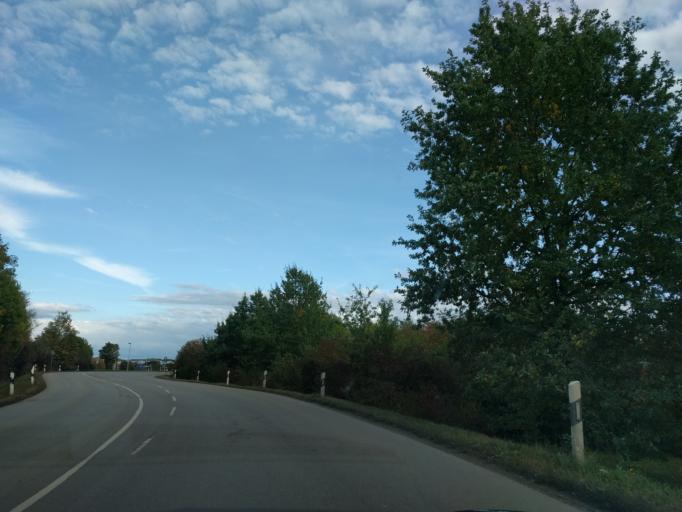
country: DE
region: Bavaria
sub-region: Lower Bavaria
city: Plattling
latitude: 48.7876
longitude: 12.8926
